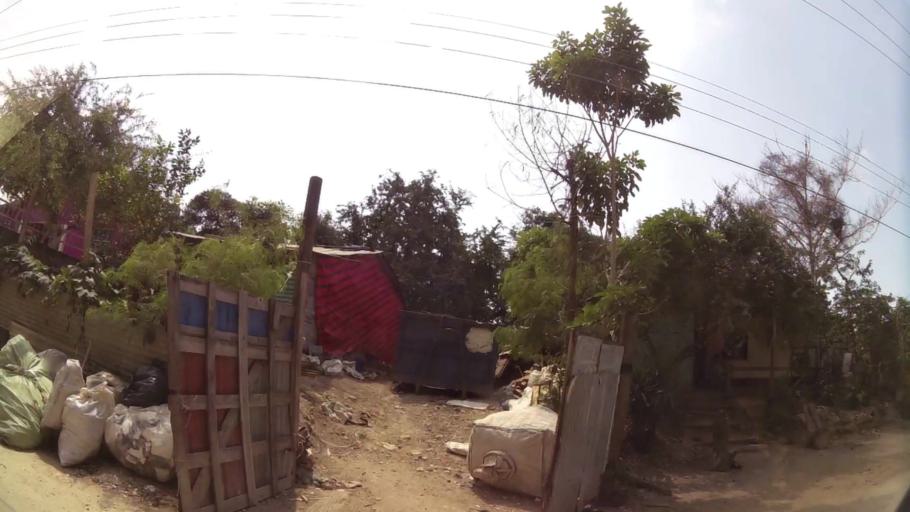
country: CO
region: Bolivar
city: Cartagena
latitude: 10.3568
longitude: -75.5013
